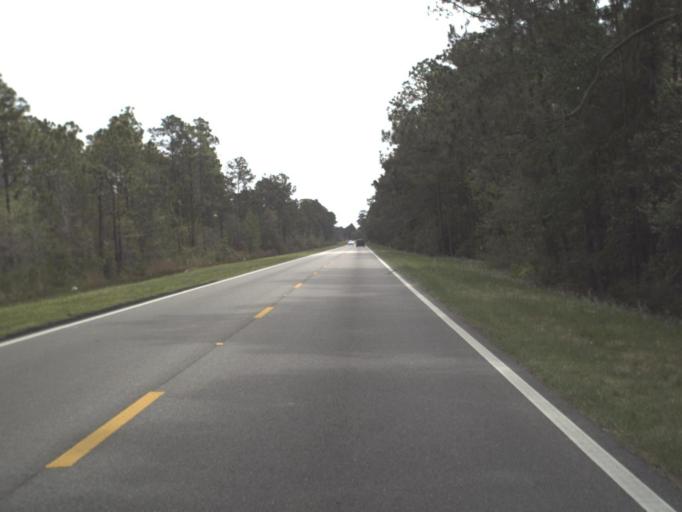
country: US
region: Florida
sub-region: Escambia County
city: Myrtle Grove
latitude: 30.3537
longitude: -87.3770
